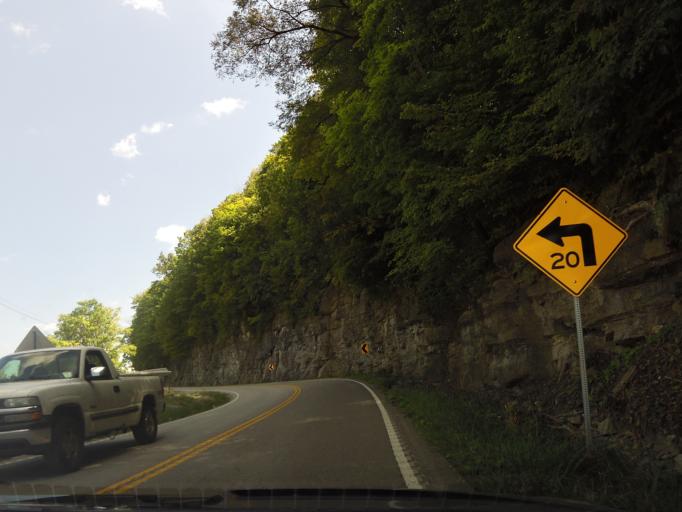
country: US
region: Kentucky
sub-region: Harlan County
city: Loyall
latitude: 36.8995
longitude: -83.3323
